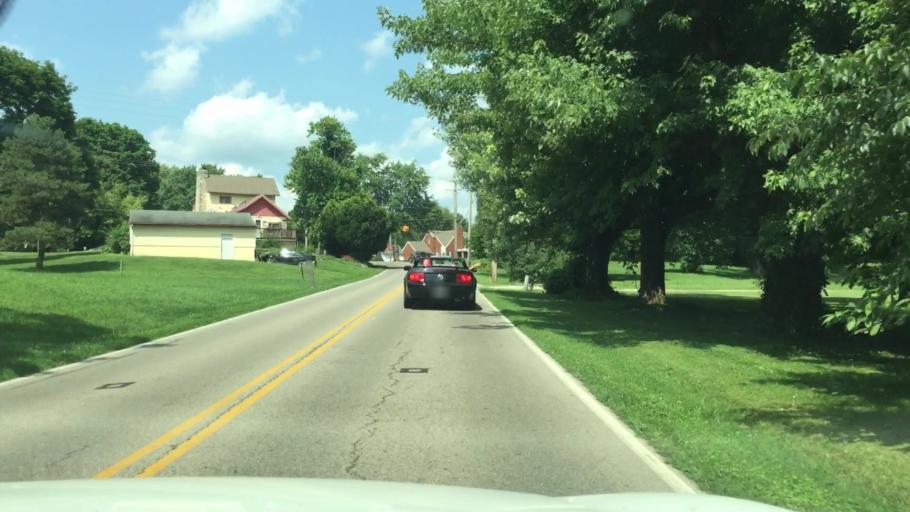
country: US
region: Ohio
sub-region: Clark County
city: Northridge
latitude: 39.9371
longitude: -83.7311
